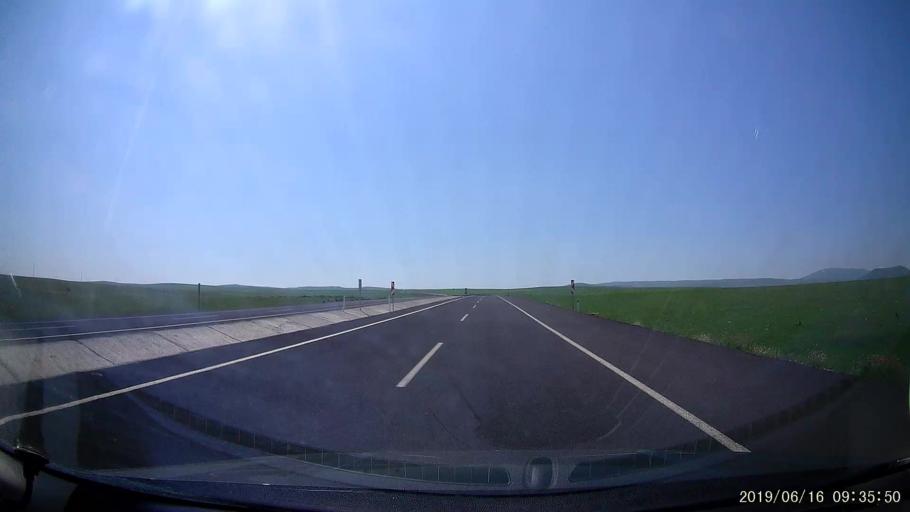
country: TR
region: Kars
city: Kars
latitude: 40.5655
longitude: 43.1626
